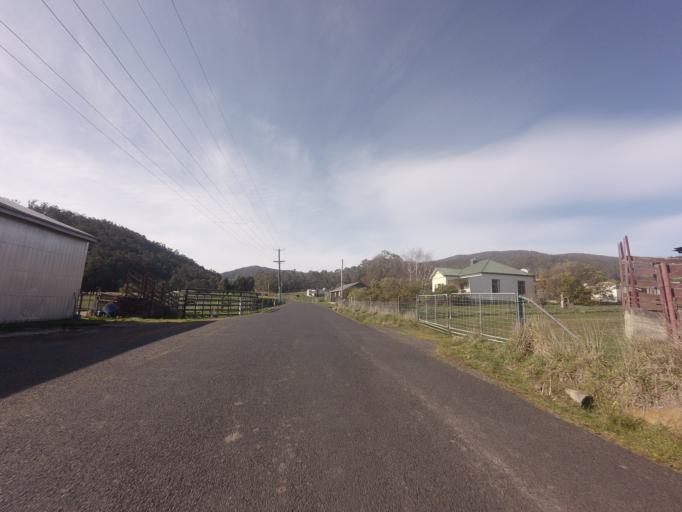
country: AU
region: Tasmania
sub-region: Huon Valley
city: Cygnet
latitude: -43.1793
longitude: 147.1336
